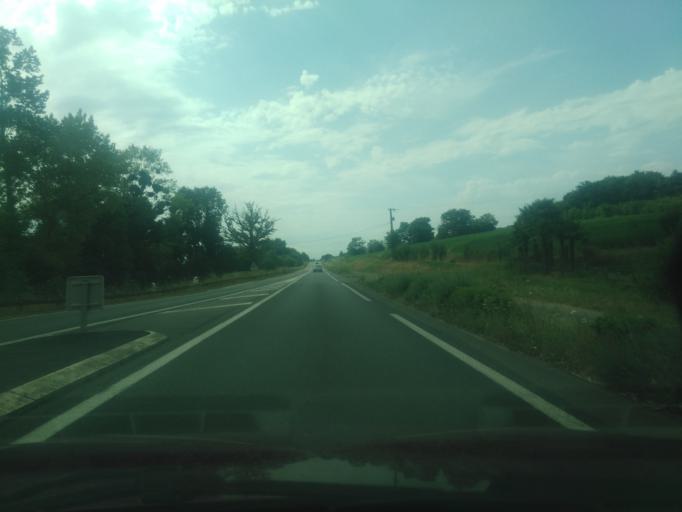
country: FR
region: Pays de la Loire
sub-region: Departement de la Vendee
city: La Chataigneraie
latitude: 46.6567
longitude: -0.7696
